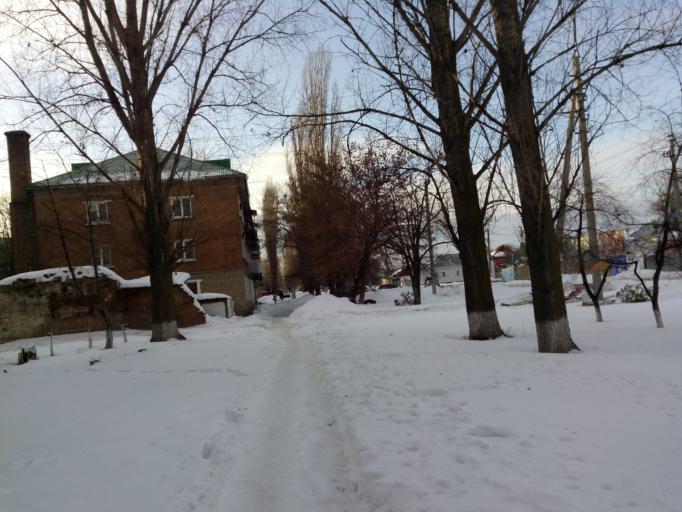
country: RU
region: Voronezj
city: Borisoglebsk
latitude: 51.3604
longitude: 42.1008
